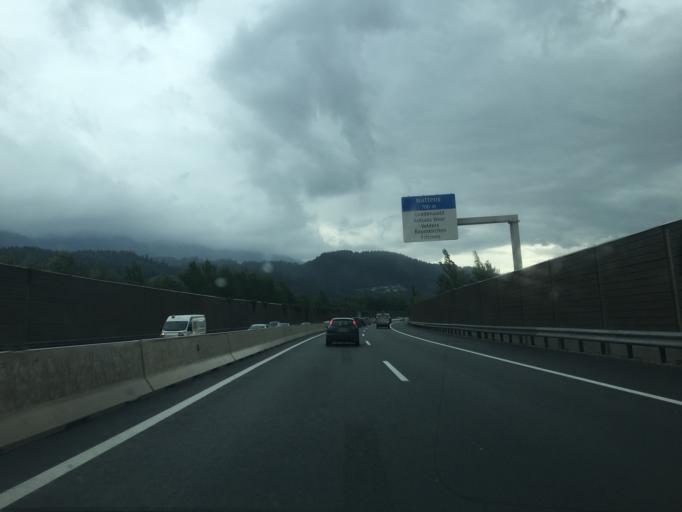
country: AT
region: Tyrol
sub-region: Politischer Bezirk Innsbruck Land
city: Baumkirchen
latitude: 47.2961
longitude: 11.5674
